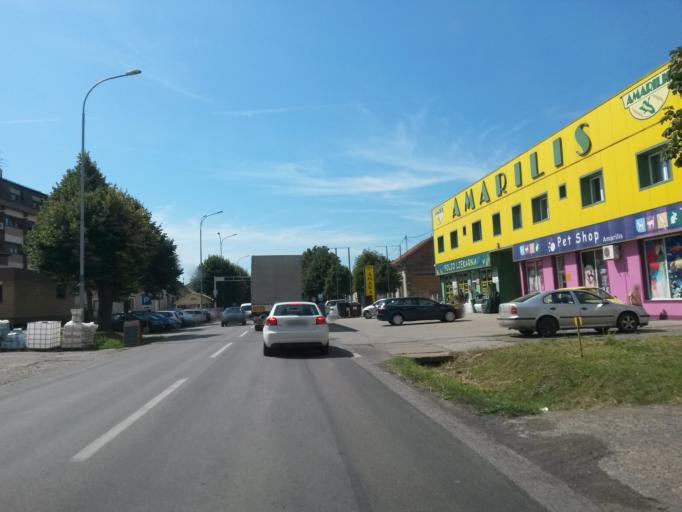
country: HR
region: Vukovarsko-Srijemska
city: Vinkovci
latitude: 45.2985
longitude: 18.8100
